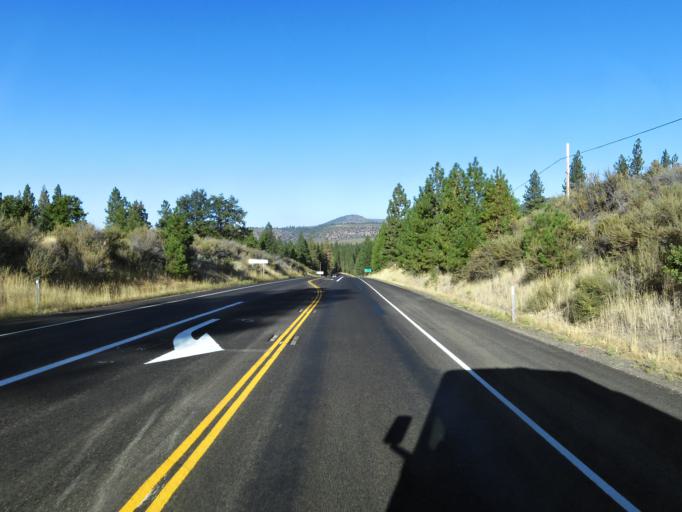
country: US
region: California
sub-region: Siskiyou County
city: Weed
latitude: 41.4442
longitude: -122.3718
